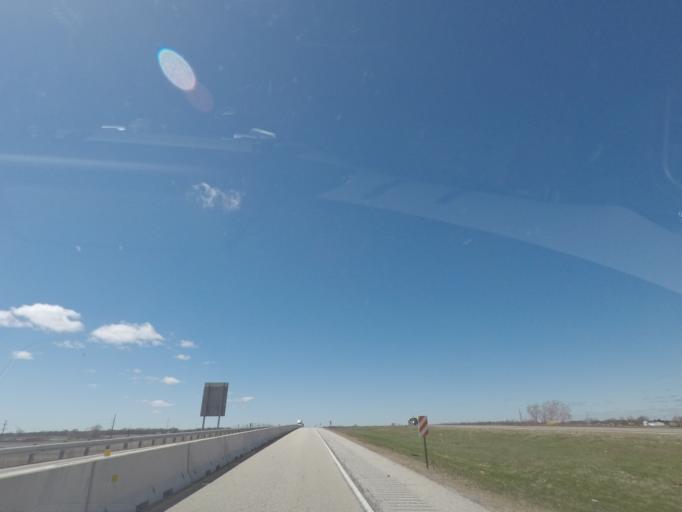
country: US
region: Illinois
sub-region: Livingston County
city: Pontiac
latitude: 40.9156
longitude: -88.6487
